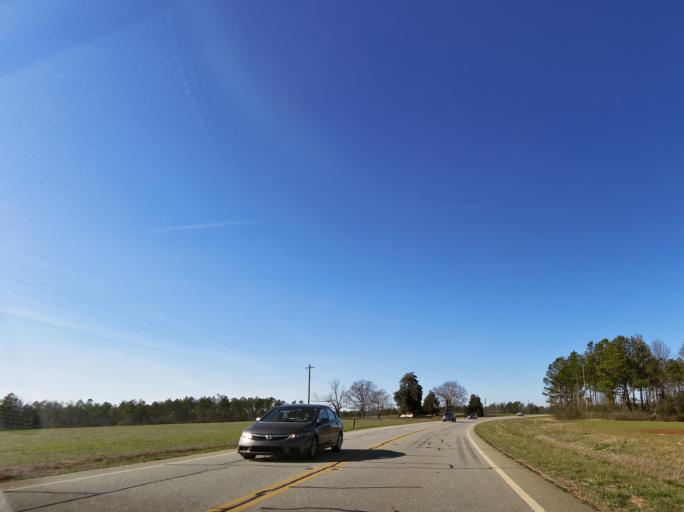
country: US
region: Georgia
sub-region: Lamar County
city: Barnesville
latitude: 32.8902
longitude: -84.1048
